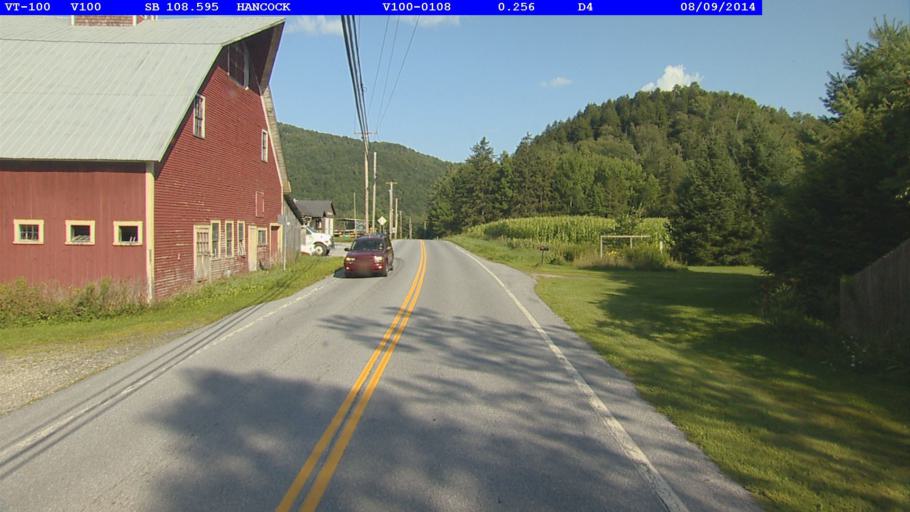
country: US
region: Vermont
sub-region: Orange County
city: Randolph
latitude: 43.9138
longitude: -72.8375
